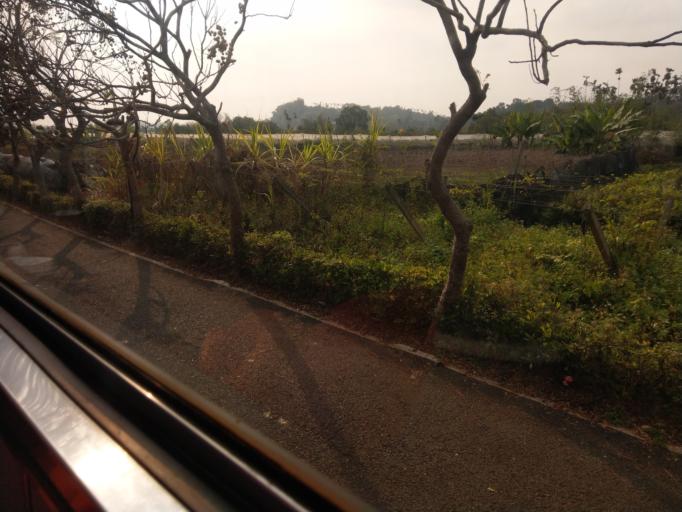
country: TW
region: Taiwan
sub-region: Chiayi
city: Jiayi Shi
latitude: 23.5162
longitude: 120.5468
